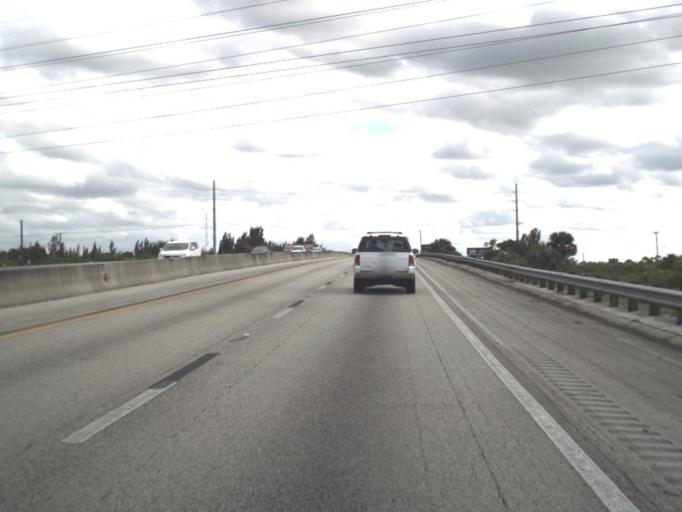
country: US
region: Florida
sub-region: Saint Lucie County
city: Fort Pierce South
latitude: 27.3825
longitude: -80.3880
